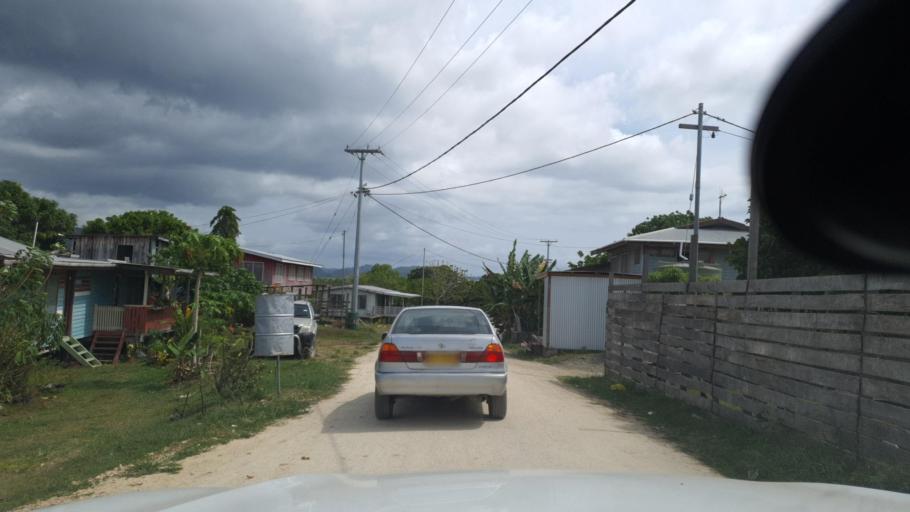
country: SB
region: Guadalcanal
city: Honiara
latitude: -9.4272
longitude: 159.9278
